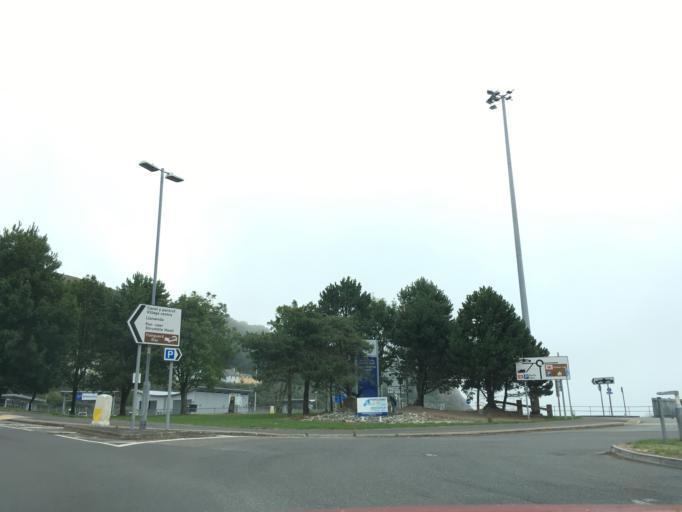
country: GB
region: Wales
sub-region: Pembrokeshire
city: Goodwick
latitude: 52.0032
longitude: -4.9936
